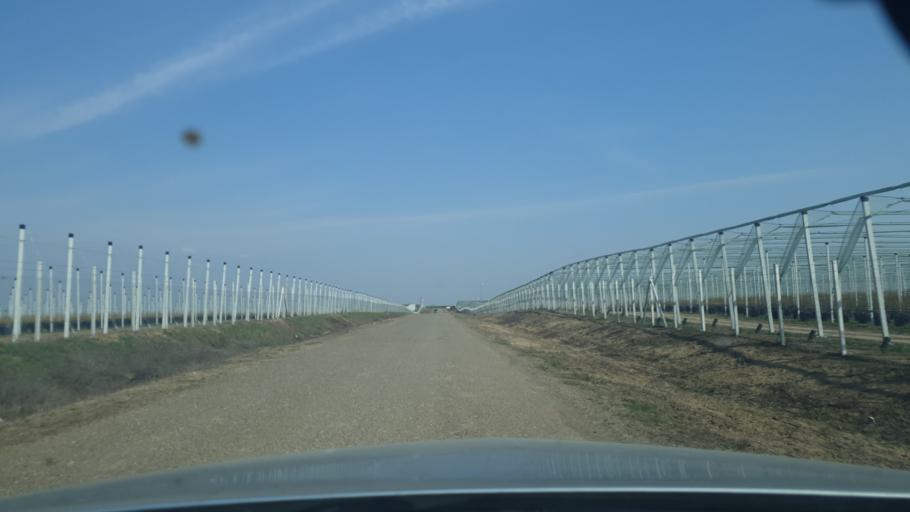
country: RS
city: Putinci
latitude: 45.0439
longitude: 19.9519
